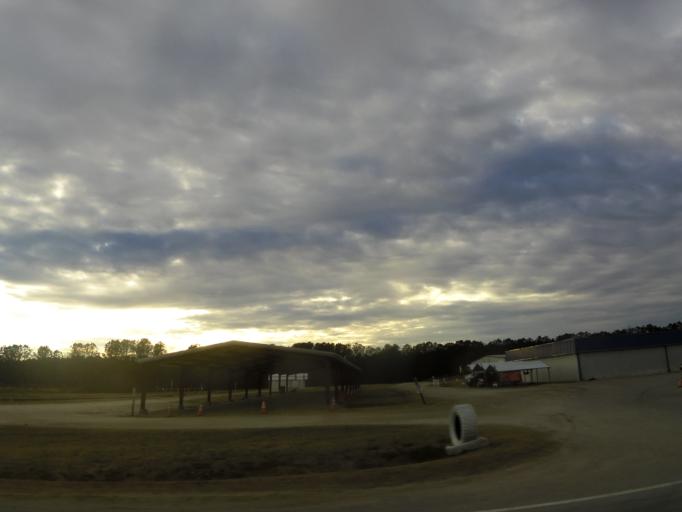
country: US
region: North Carolina
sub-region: Nash County
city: Sharpsburg
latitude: 35.8989
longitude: -77.8256
